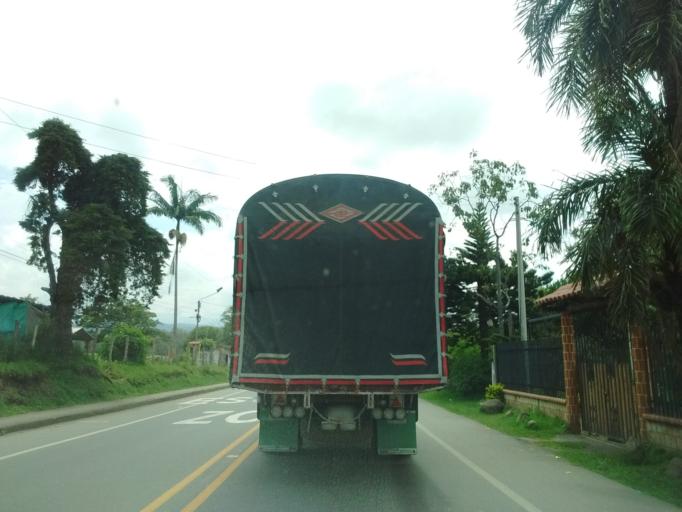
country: CO
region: Cauca
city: Cajibio
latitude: 2.5227
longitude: -76.5489
